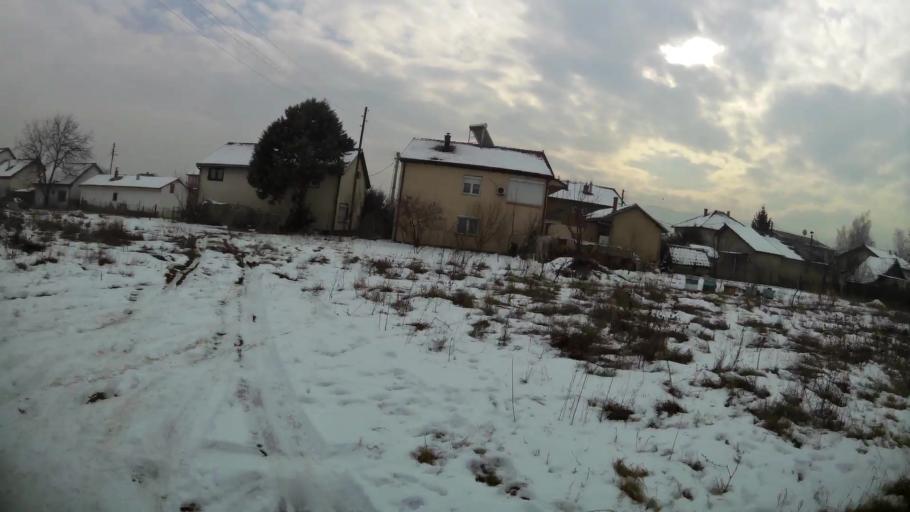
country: MK
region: Saraj
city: Saraj
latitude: 42.0235
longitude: 21.3498
